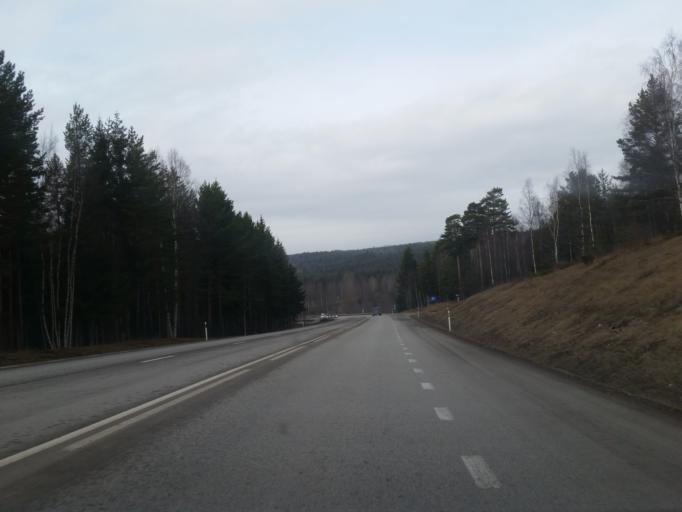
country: SE
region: Dalarna
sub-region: Rattviks Kommun
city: Vikarbyn
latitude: 60.9101
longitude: 15.0563
